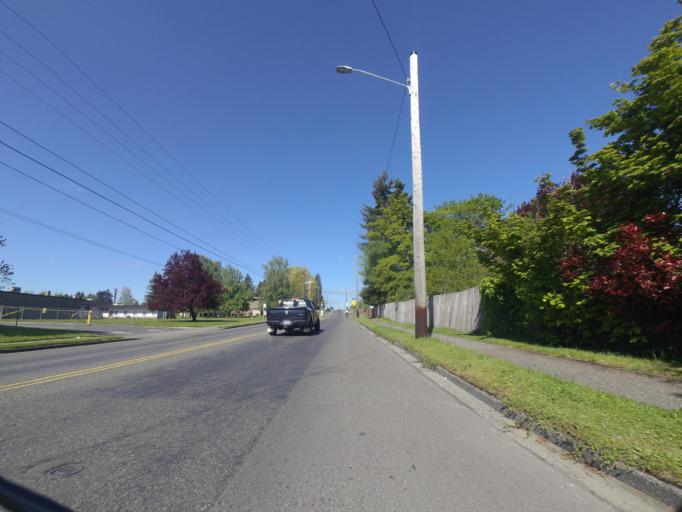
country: US
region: Washington
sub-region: Pierce County
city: Midland
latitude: 47.2065
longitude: -122.4269
